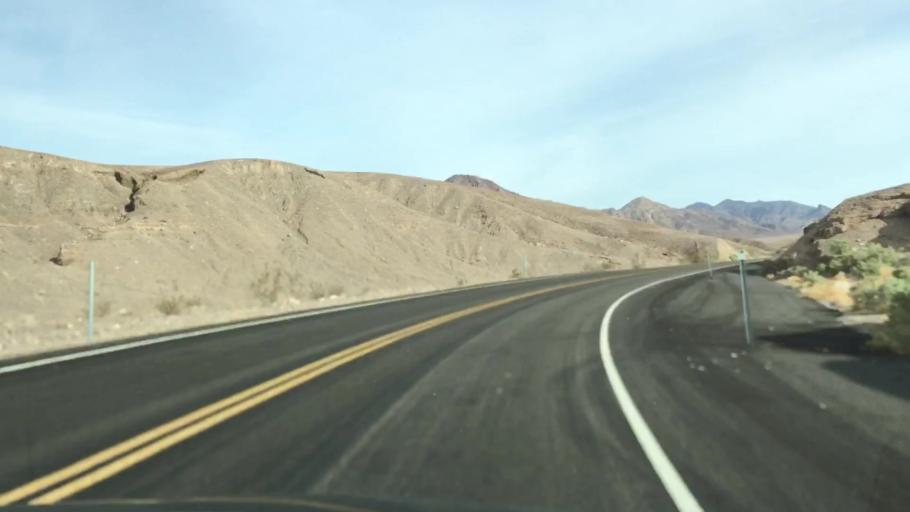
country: US
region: Nevada
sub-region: Nye County
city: Beatty
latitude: 36.6730
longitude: -117.0130
